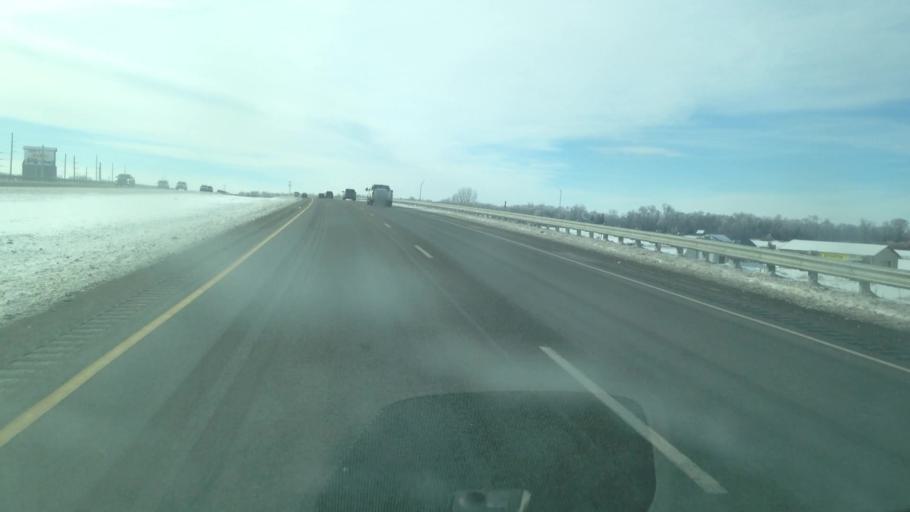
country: US
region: Idaho
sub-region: Madison County
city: Rexburg
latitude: 43.7640
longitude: -111.8429
